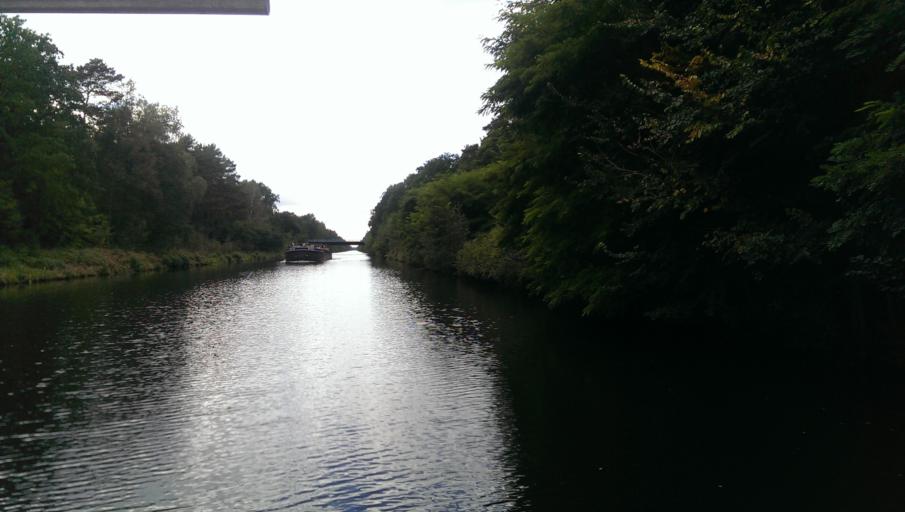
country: DE
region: Brandenburg
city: Marienwerder
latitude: 52.8465
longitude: 13.5279
